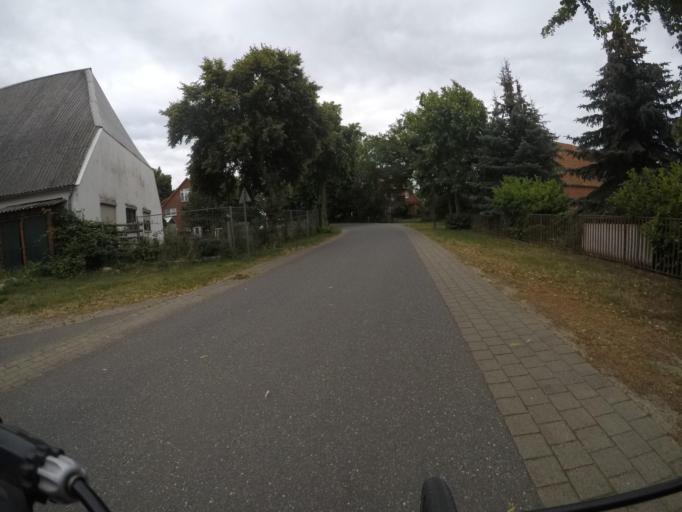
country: DE
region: Lower Saxony
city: Neu Darchau
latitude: 53.2578
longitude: 10.9193
